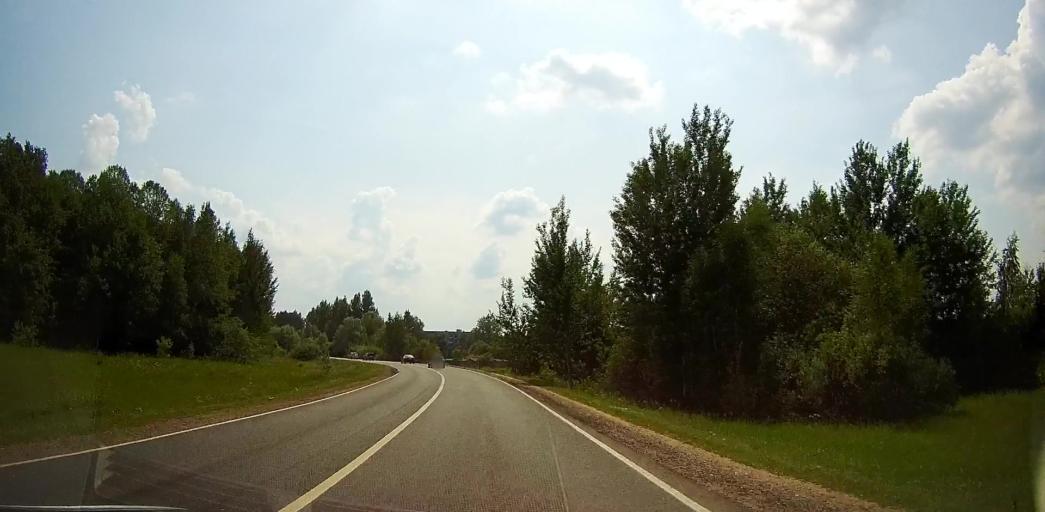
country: RU
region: Moskovskaya
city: Malino
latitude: 55.0952
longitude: 38.1650
